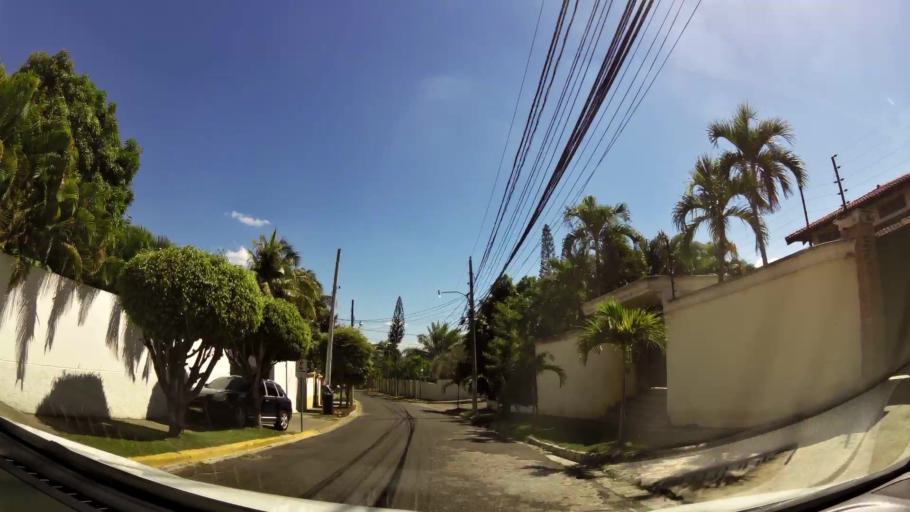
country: DO
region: Santiago
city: Santiago de los Caballeros
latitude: 19.4471
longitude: -70.6891
